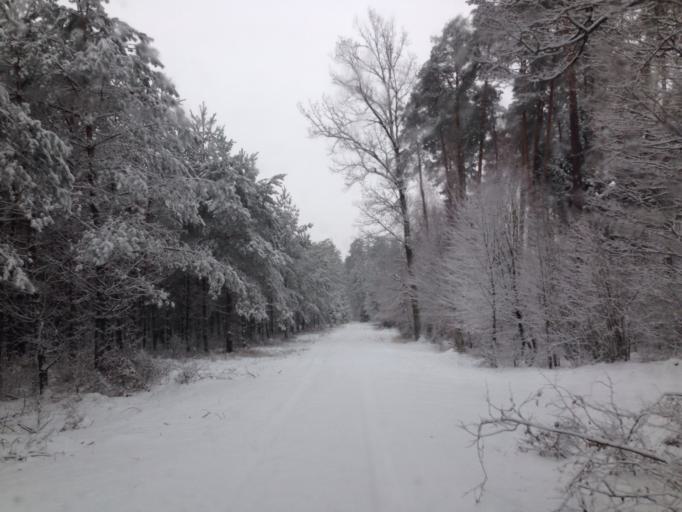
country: PL
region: Kujawsko-Pomorskie
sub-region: Powiat brodnicki
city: Gorzno
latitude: 53.1821
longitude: 19.6782
